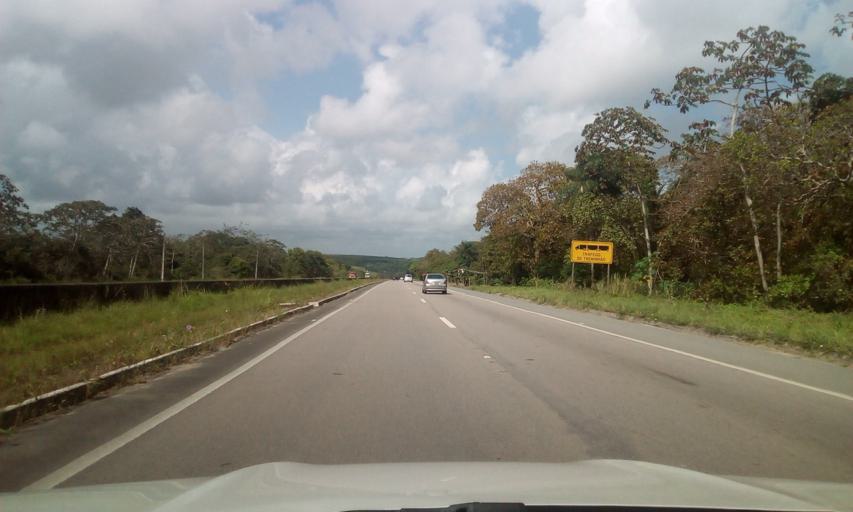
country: BR
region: Paraiba
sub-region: Alhandra
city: Alhandra
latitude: -7.4233
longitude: -34.9633
